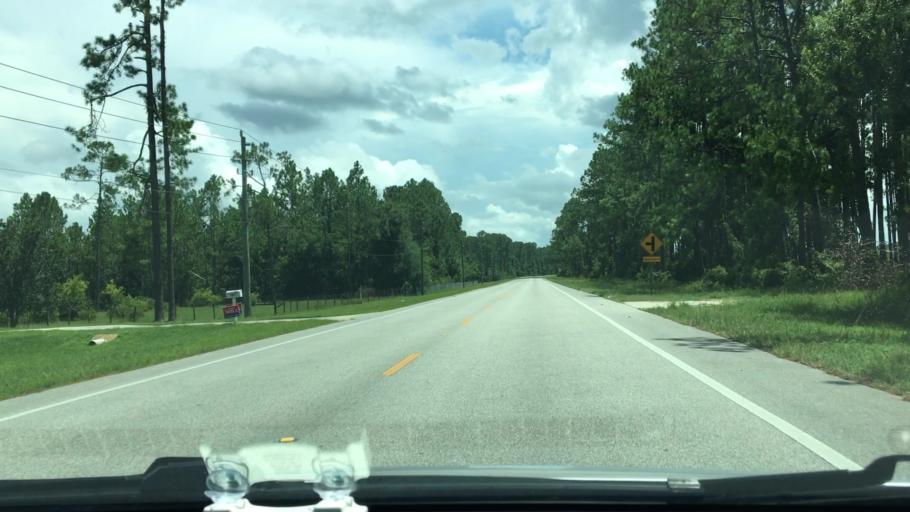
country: US
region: Florida
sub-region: Volusia County
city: Samsula-Spruce Creek
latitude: 29.0325
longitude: -81.0667
